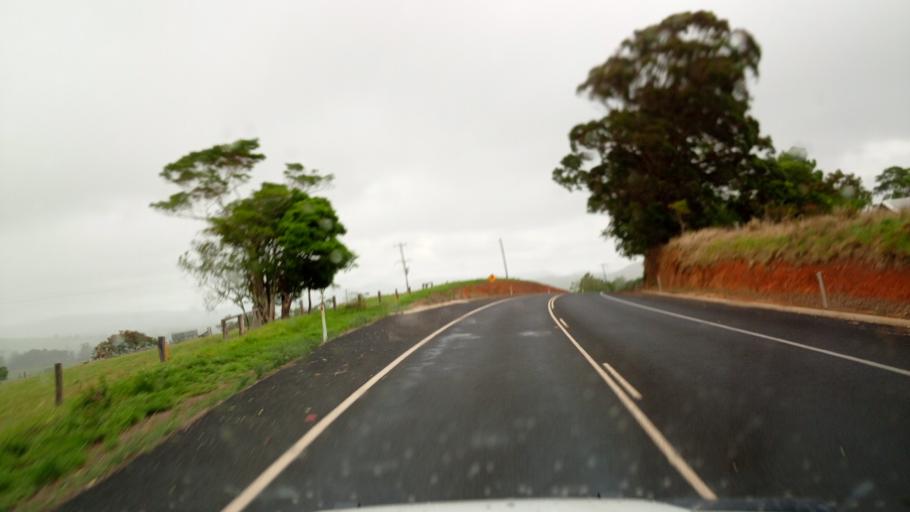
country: AU
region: Queensland
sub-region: Tablelands
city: Atherton
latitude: -17.2811
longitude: 145.5958
